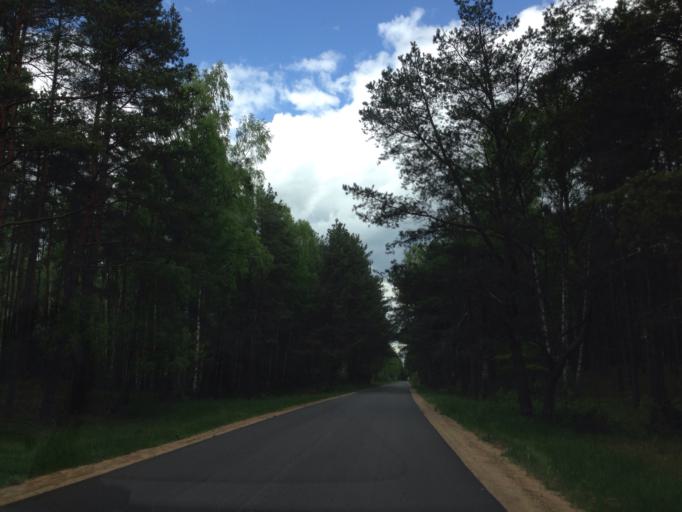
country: PL
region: Podlasie
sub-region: Powiat grajewski
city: Radzilow
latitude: 53.3479
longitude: 22.5972
